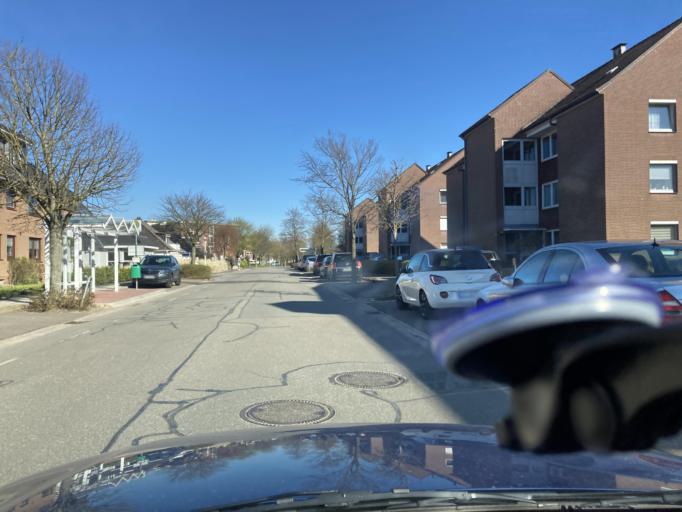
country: DE
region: Schleswig-Holstein
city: Busum
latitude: 54.1348
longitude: 8.8518
